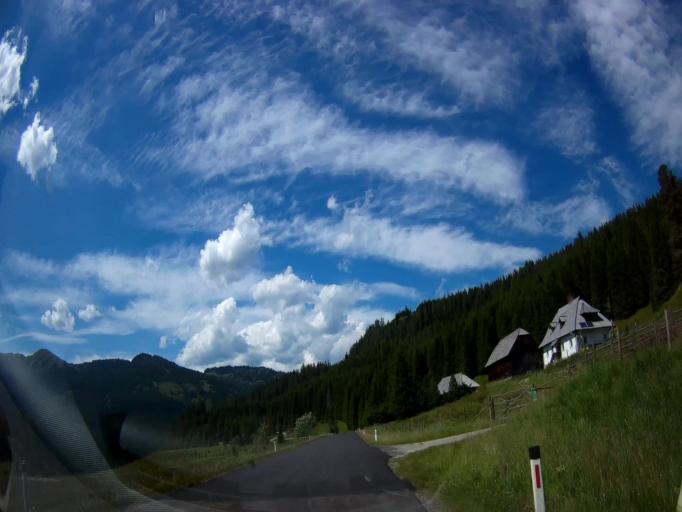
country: AT
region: Styria
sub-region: Politischer Bezirk Murau
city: Stadl an der Mur
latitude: 46.9695
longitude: 14.0169
